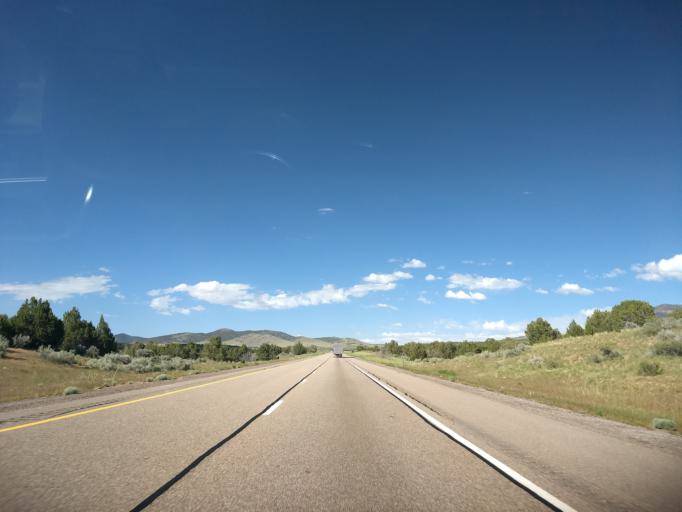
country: US
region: Utah
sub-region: Millard County
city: Fillmore
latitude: 39.1618
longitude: -112.2215
